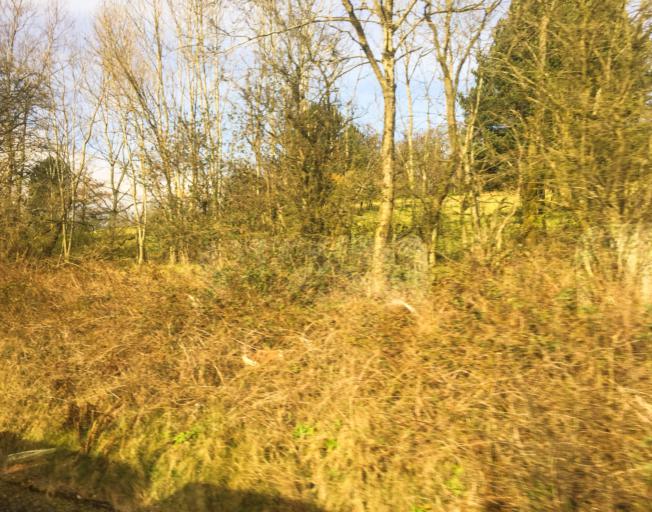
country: GB
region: Scotland
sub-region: East Dunbartonshire
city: Bearsden
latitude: 55.8948
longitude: -4.3174
